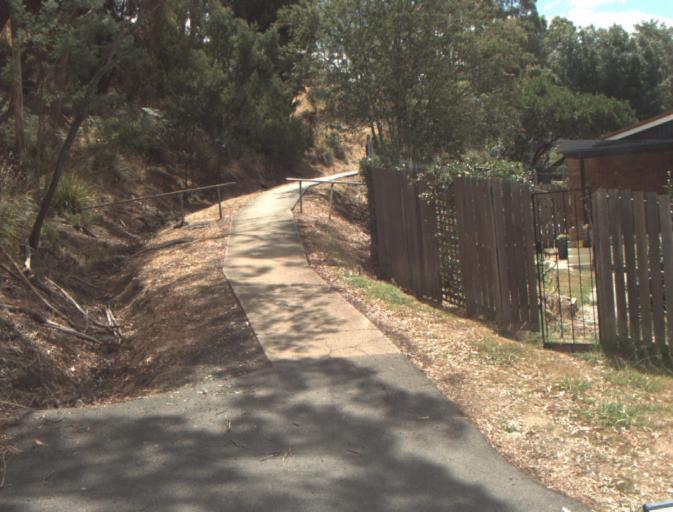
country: AU
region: Tasmania
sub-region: Launceston
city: Launceston
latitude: -41.4365
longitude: 147.1109
